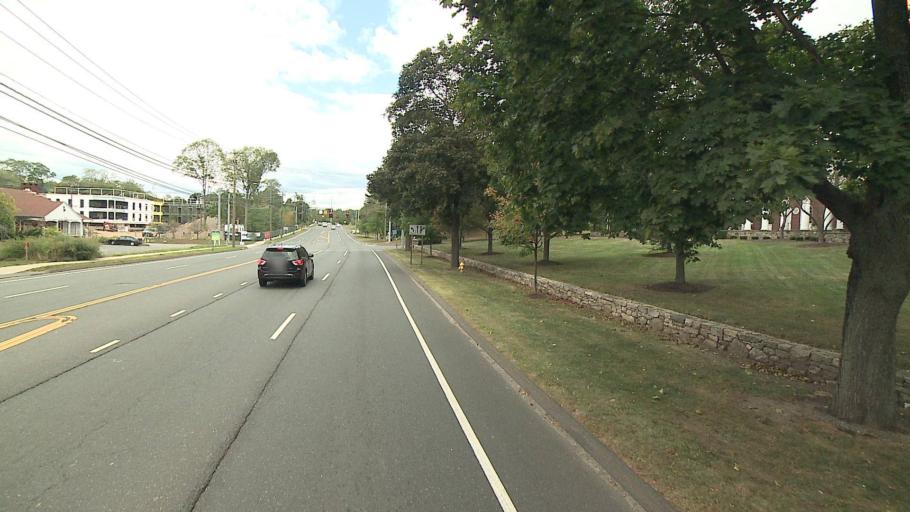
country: US
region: Connecticut
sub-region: Fairfield County
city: Wilton
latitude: 41.1895
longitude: -73.4263
